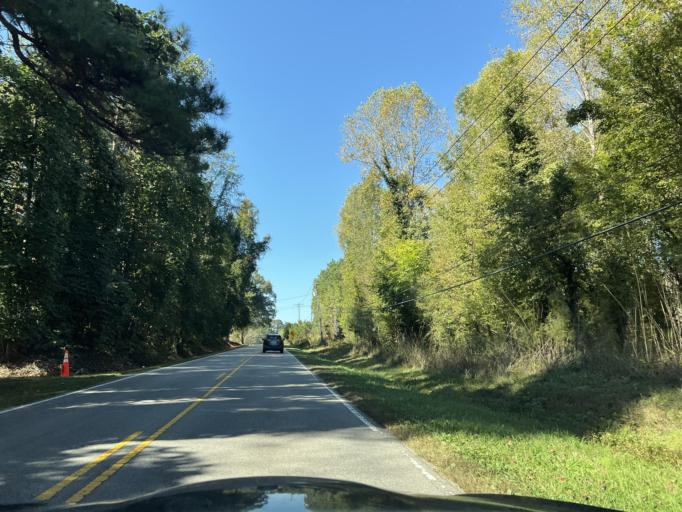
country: US
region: North Carolina
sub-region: Wake County
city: Garner
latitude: 35.6900
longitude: -78.5368
